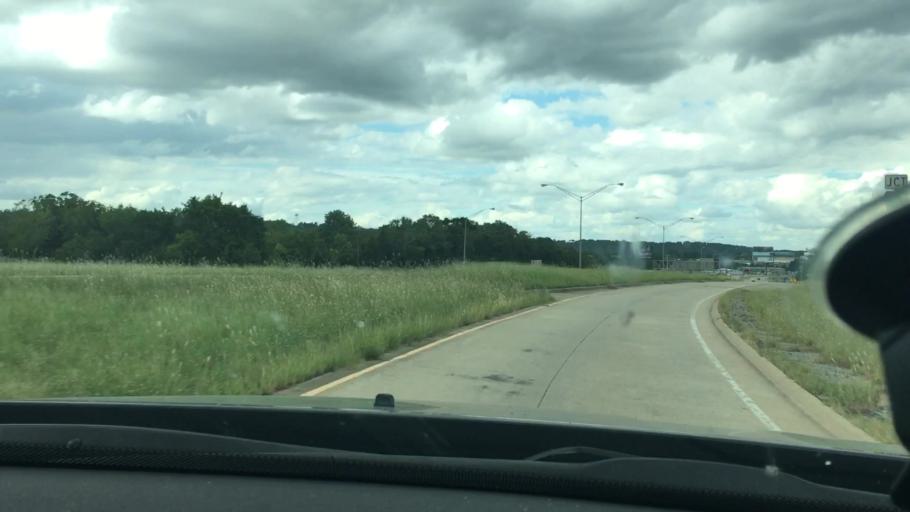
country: US
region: Oklahoma
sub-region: Okmulgee County
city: Henryetta
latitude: 35.4349
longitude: -95.9705
